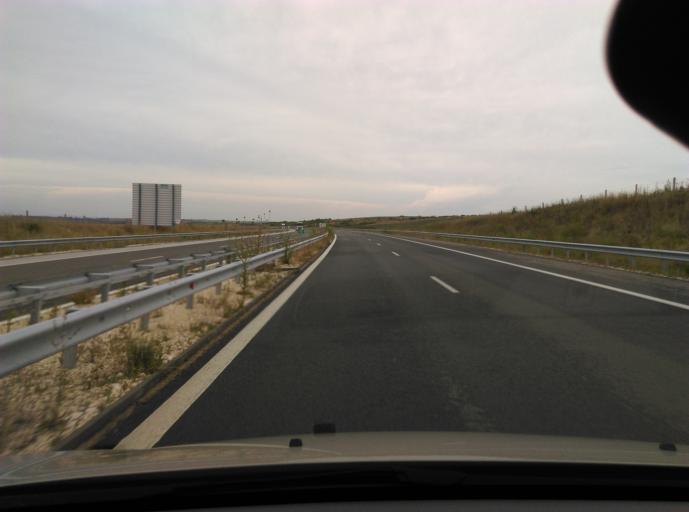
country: BG
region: Stara Zagora
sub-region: Obshtina Chirpan
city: Chirpan
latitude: 42.1171
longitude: 25.4010
